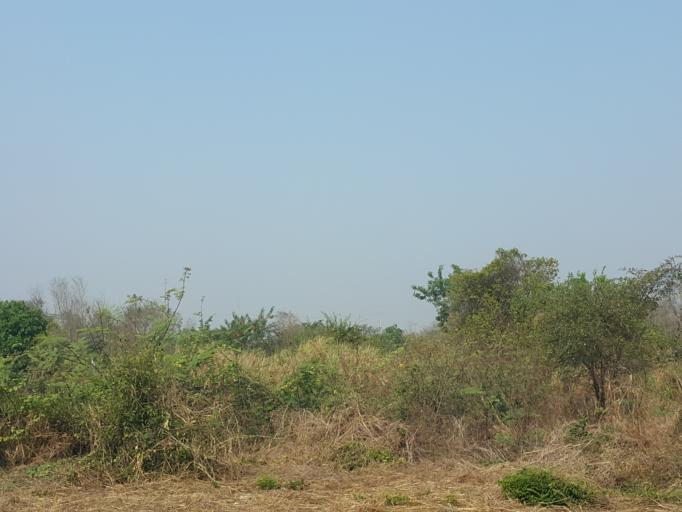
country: TH
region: Chiang Mai
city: San Kamphaeng
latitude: 18.7835
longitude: 99.0730
